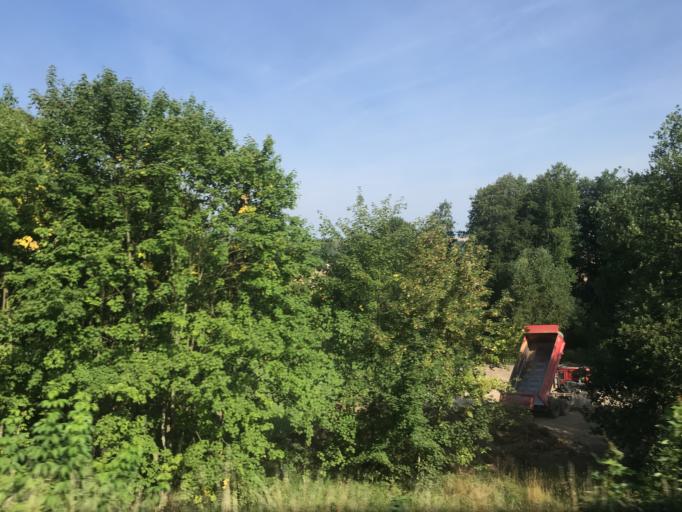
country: CZ
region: Jihocesky
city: Chotoviny
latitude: 49.5105
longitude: 14.6636
